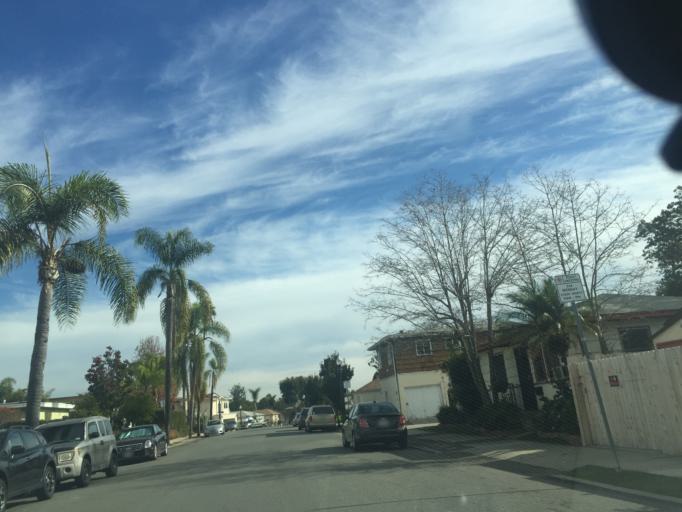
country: US
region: California
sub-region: San Diego County
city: Lemon Grove
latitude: 32.7609
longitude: -117.0854
